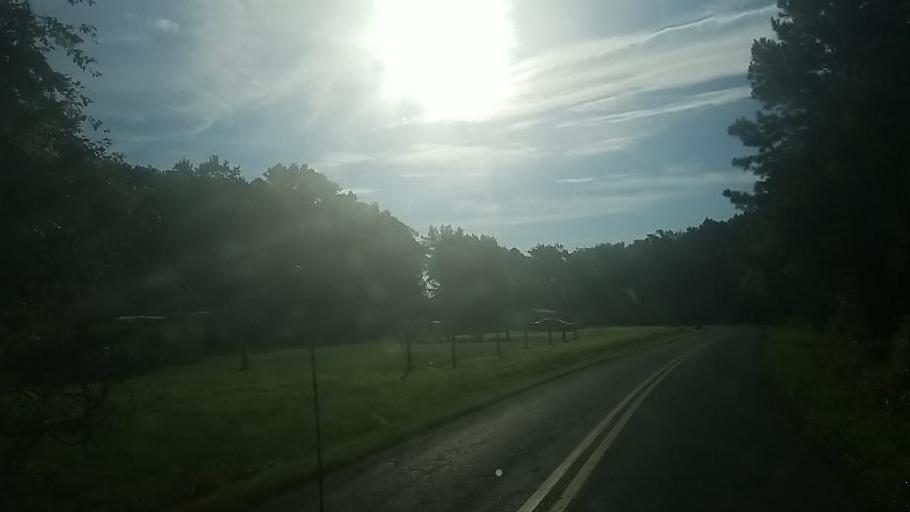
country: US
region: Maryland
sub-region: Worcester County
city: West Ocean City
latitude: 38.3127
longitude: -75.1598
